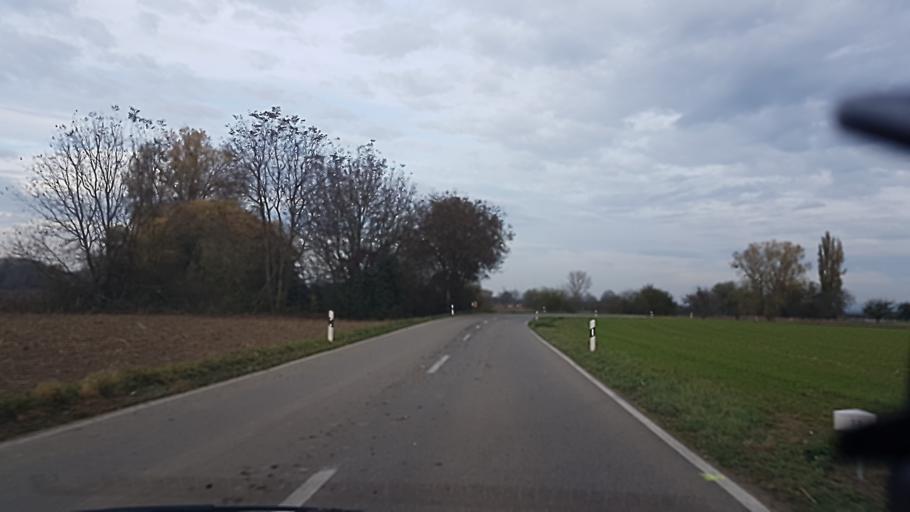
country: DE
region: Baden-Wuerttemberg
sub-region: Freiburg Region
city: Wyhl
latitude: 48.1755
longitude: 7.6583
